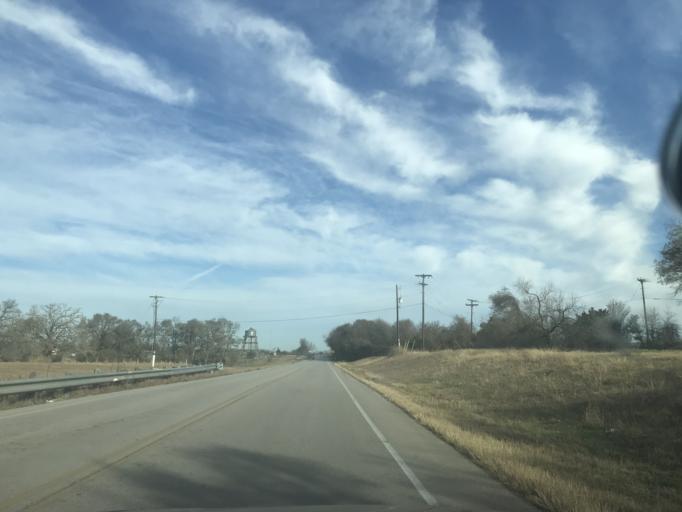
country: US
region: Texas
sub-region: Travis County
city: Manor
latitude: 30.2875
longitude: -97.5228
